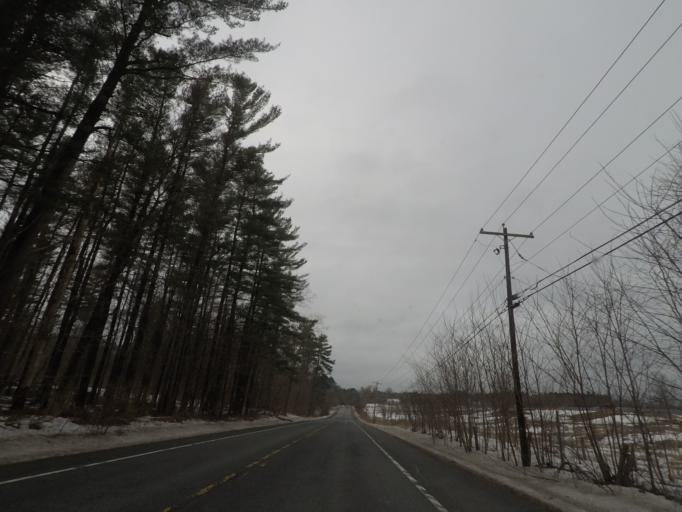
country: US
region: New York
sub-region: Schenectady County
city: Rotterdam
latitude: 42.7279
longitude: -73.9667
